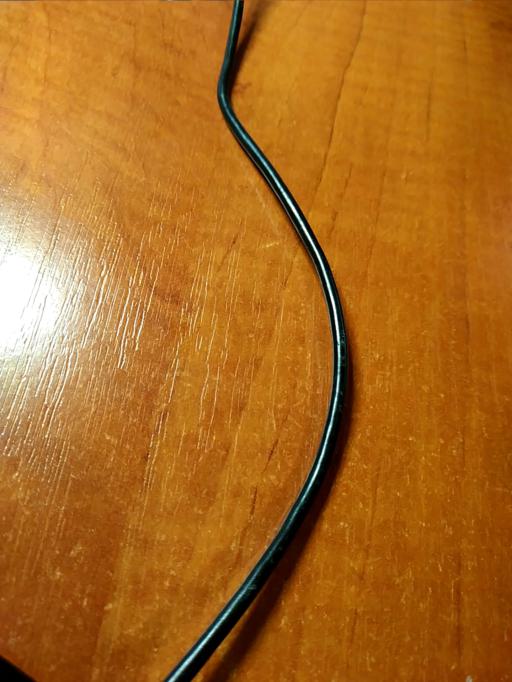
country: RU
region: Smolensk
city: Dorogobuzh
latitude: 54.8503
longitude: 33.3218
